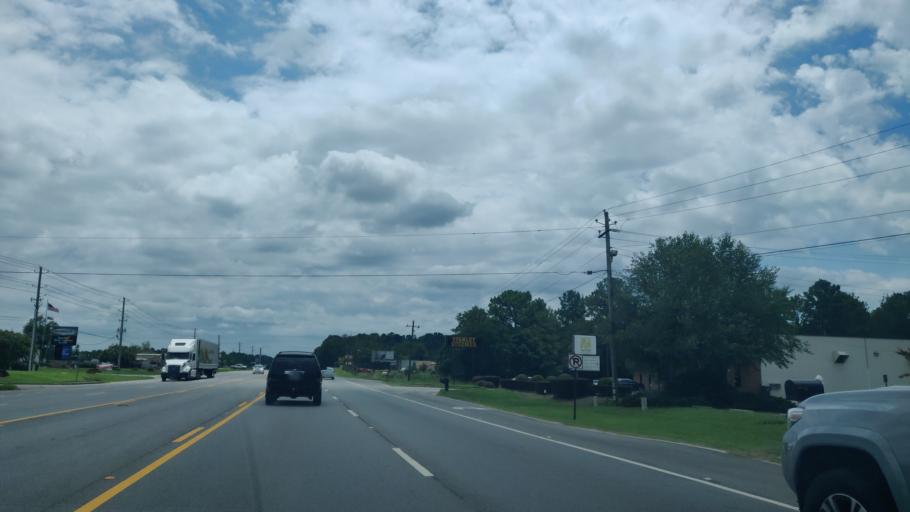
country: US
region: Georgia
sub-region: Dougherty County
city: Albany
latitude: 31.6329
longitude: -84.2430
